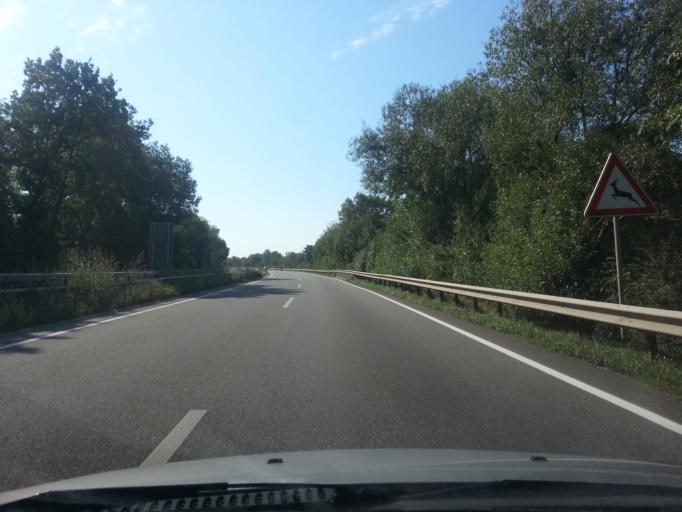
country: DE
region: Rheinland-Pfalz
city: Worms
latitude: 49.6167
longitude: 8.3683
